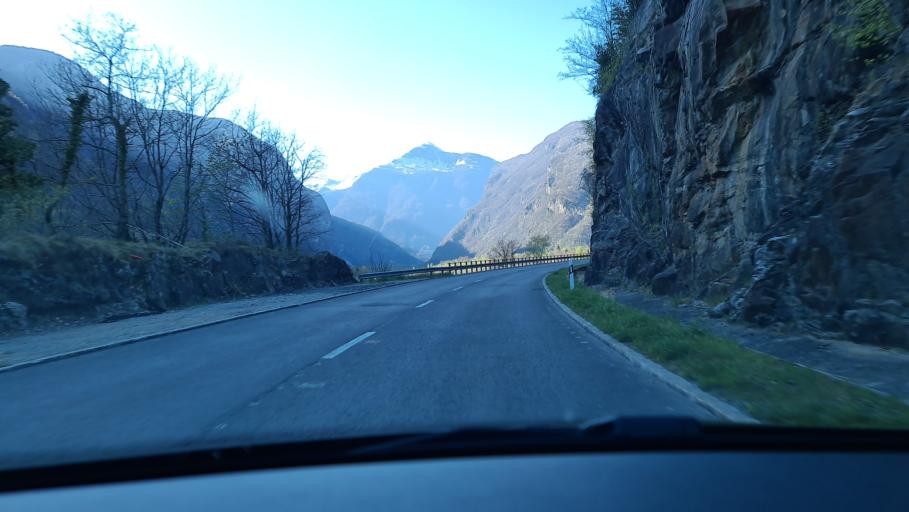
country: CH
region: Ticino
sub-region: Vallemaggia District
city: Cevio
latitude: 46.2754
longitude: 8.6757
